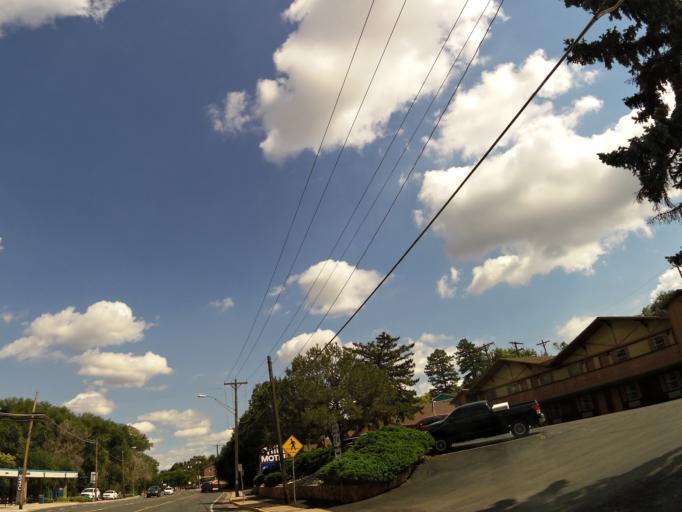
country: US
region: Colorado
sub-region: El Paso County
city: Manitou Springs
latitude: 38.8574
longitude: -104.9107
